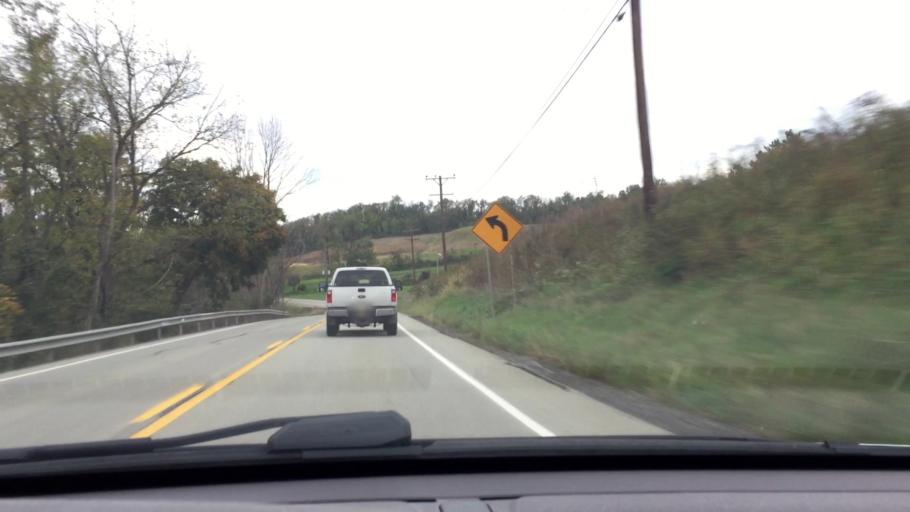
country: US
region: Pennsylvania
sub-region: Washington County
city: Canonsburg
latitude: 40.2341
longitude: -80.1685
